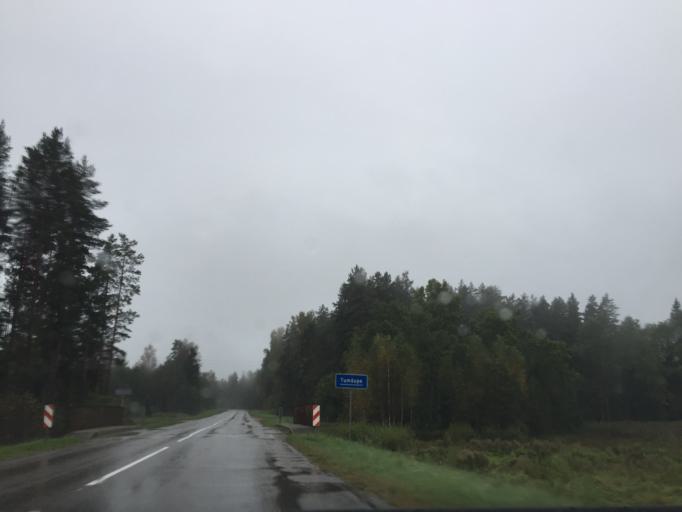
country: LV
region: Incukalns
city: Incukalns
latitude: 57.0293
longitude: 24.6827
